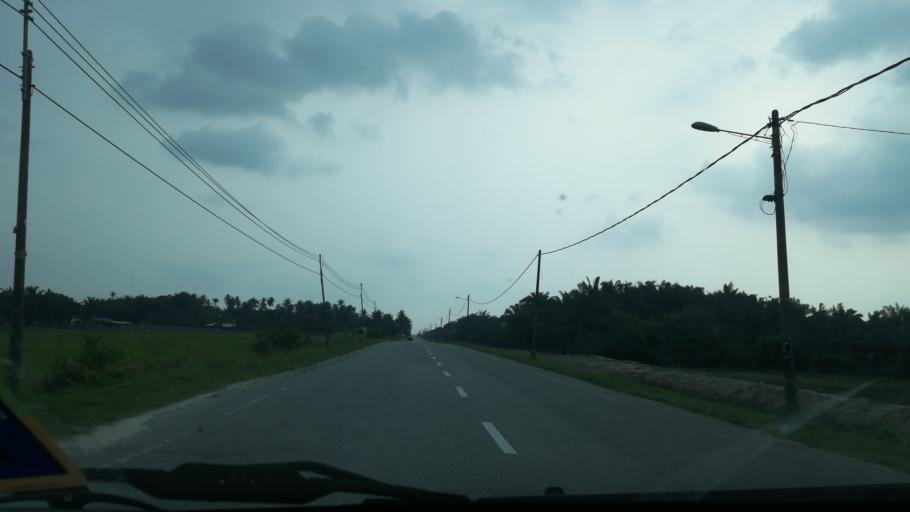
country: MY
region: Perak
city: Teluk Intan
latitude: 4.1174
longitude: 101.0748
